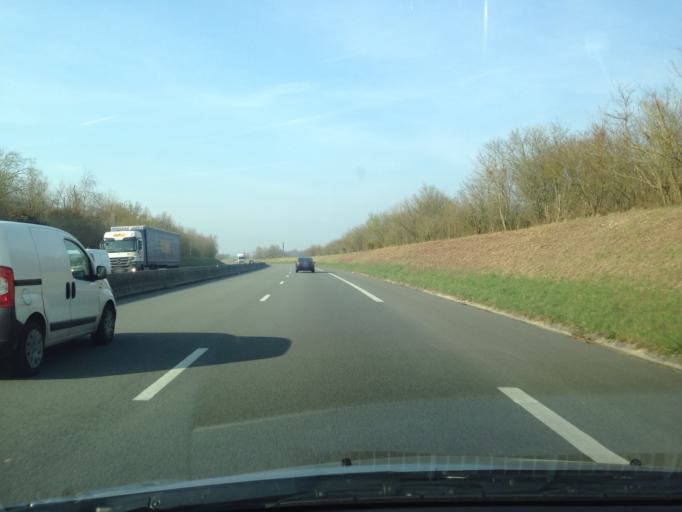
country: FR
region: Nord-Pas-de-Calais
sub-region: Departement du Pas-de-Calais
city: Saint-Josse
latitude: 50.4649
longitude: 1.7033
